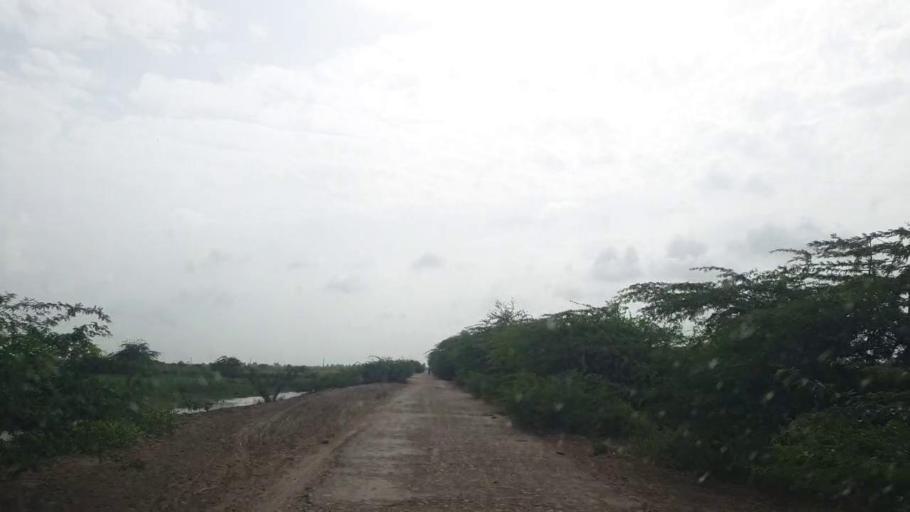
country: PK
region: Sindh
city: Tando Bago
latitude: 24.7976
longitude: 68.9956
